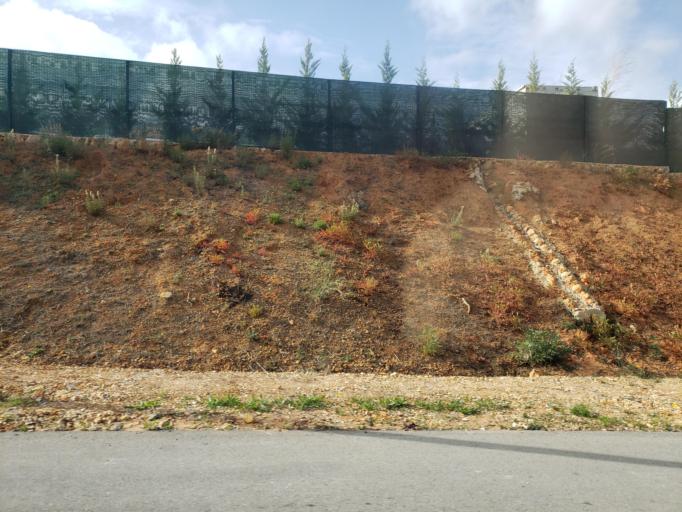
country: PT
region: Faro
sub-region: Portimao
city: Alvor
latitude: 37.1575
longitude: -8.5704
